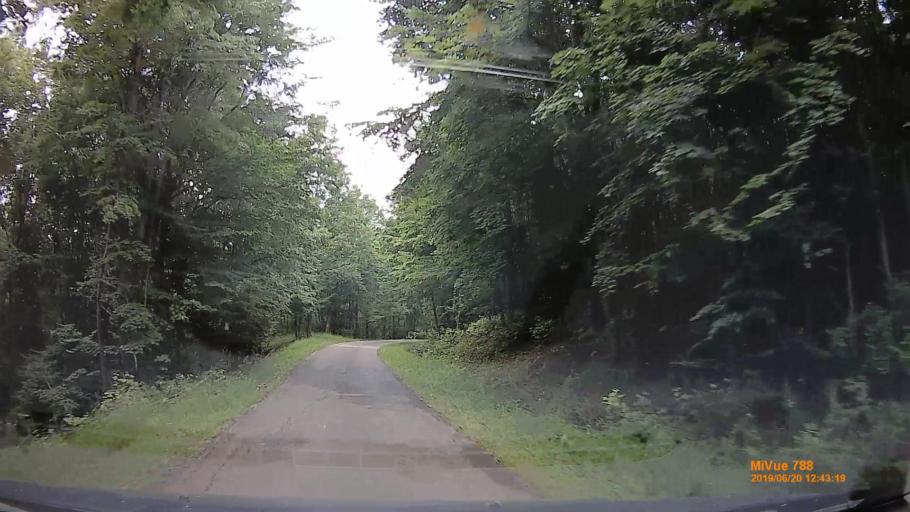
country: HU
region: Baranya
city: Hosszuheteny
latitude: 46.2002
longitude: 18.3564
